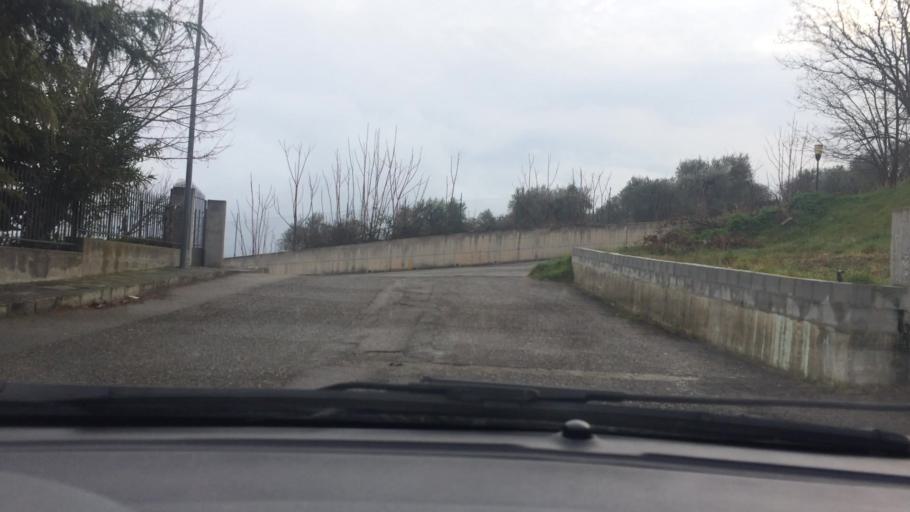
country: IT
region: Basilicate
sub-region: Provincia di Matera
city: San Mauro Forte
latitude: 40.4902
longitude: 16.2424
